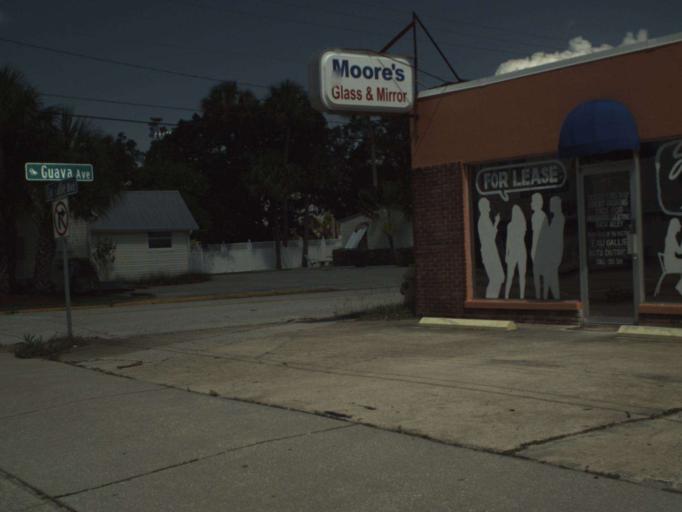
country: US
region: Florida
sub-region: Brevard County
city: Indian Harbour Beach
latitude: 28.1301
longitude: -80.6278
